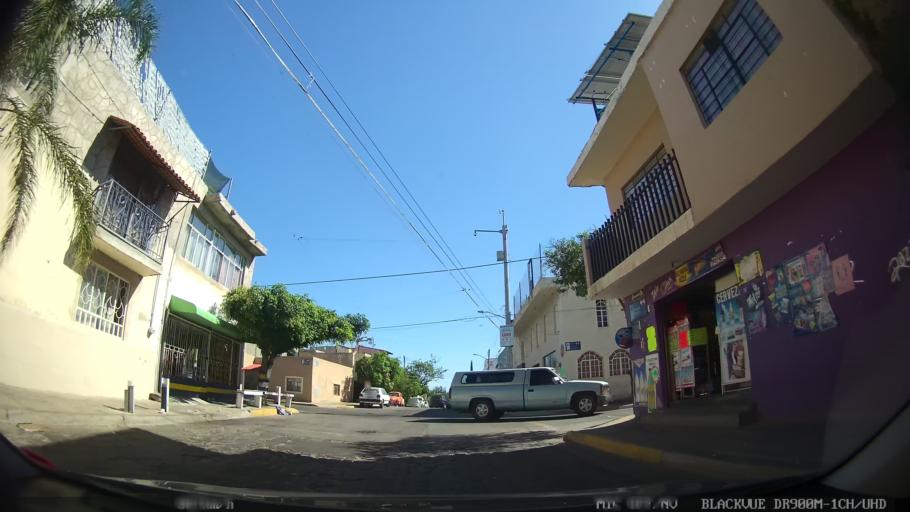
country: MX
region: Jalisco
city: Tlaquepaque
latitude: 20.6846
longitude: -103.2768
